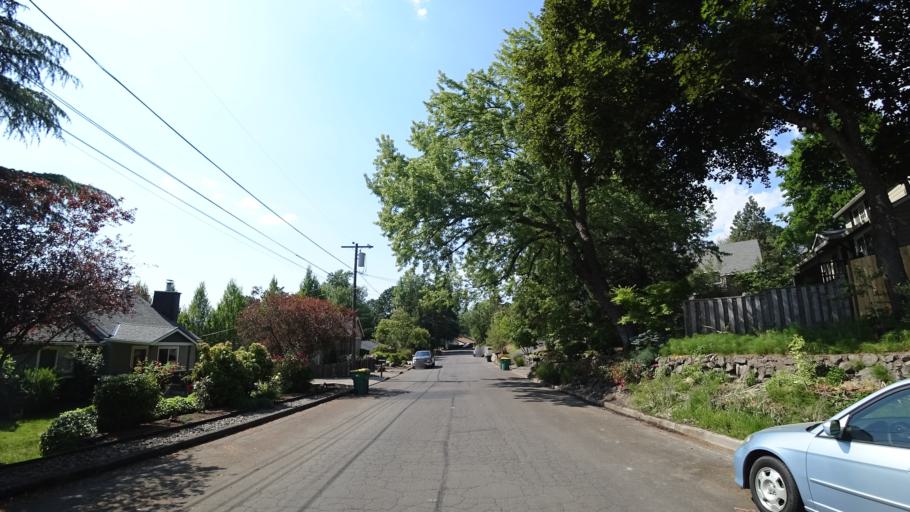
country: US
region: Oregon
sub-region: Washington County
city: Metzger
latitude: 45.4518
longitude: -122.7477
